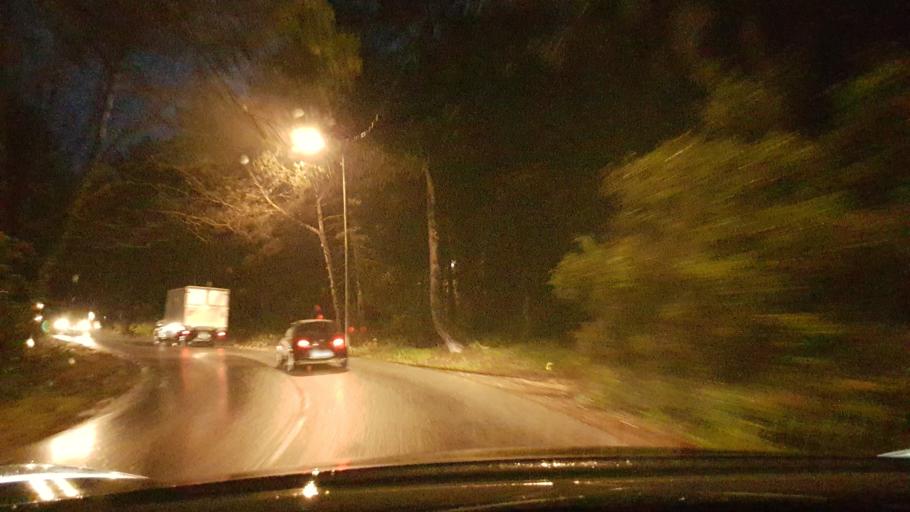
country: FR
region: Provence-Alpes-Cote d'Azur
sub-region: Departement des Alpes-Maritimes
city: Vallauris
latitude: 43.5960
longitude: 7.0383
